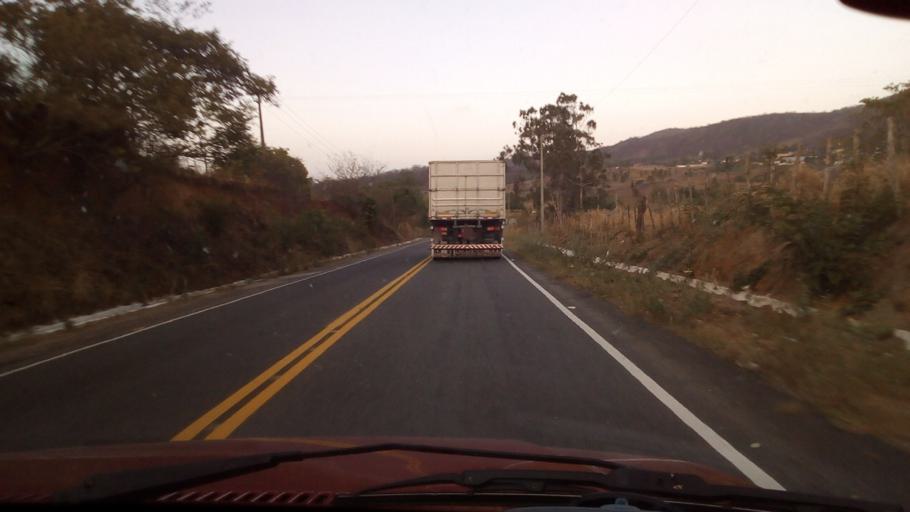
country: BR
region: Paraiba
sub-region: Bananeiras
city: Solanea
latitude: -6.7248
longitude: -35.5519
